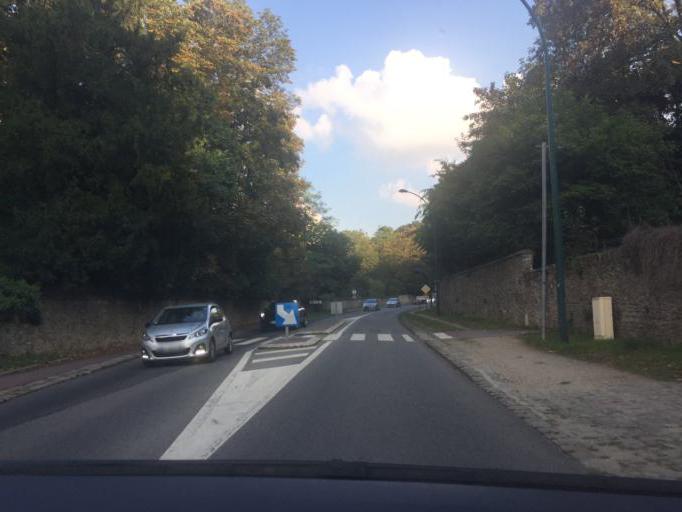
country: FR
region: Ile-de-France
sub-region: Departement des Yvelines
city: Jouy-en-Josas
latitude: 48.7620
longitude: 2.1701
